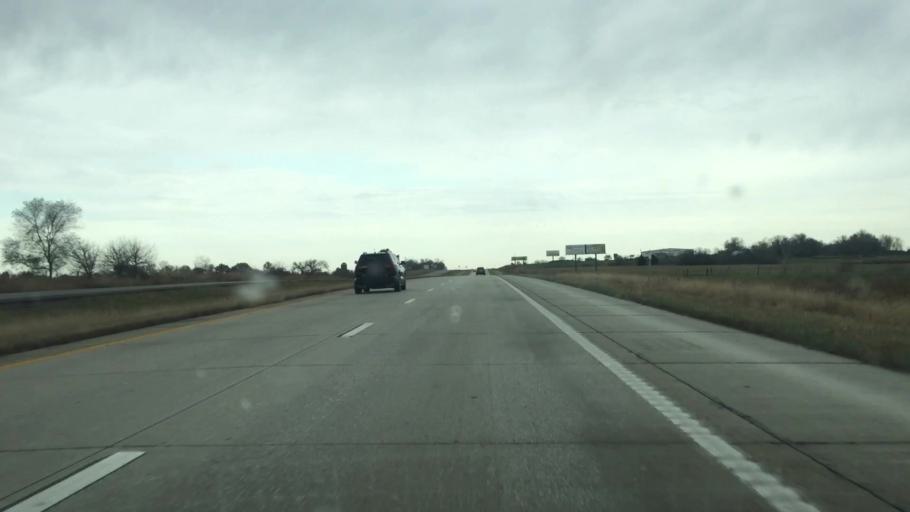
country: US
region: Missouri
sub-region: Saint Clair County
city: Osceola
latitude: 38.1598
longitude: -93.7226
